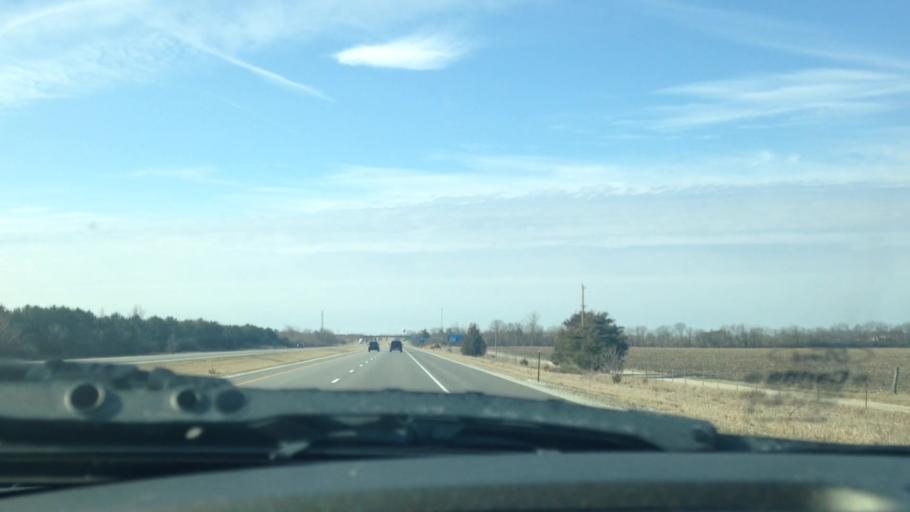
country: US
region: Illinois
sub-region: Ford County
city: Paxton
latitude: 40.4848
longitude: -88.0981
